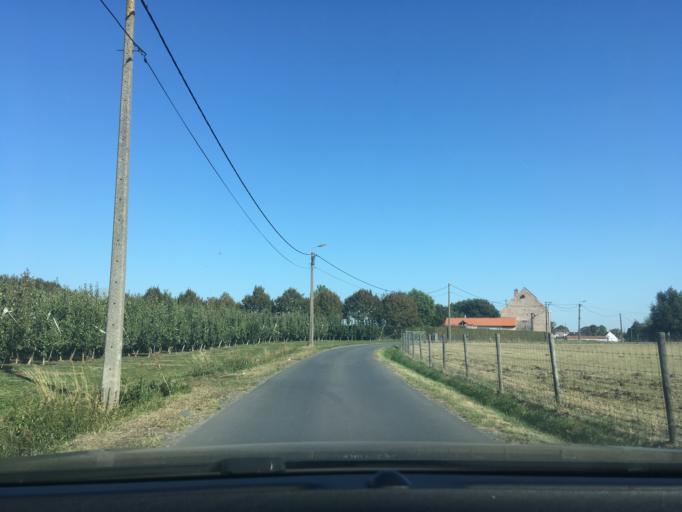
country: BE
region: Flanders
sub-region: Provincie West-Vlaanderen
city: Ledegem
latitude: 50.8806
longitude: 3.1434
